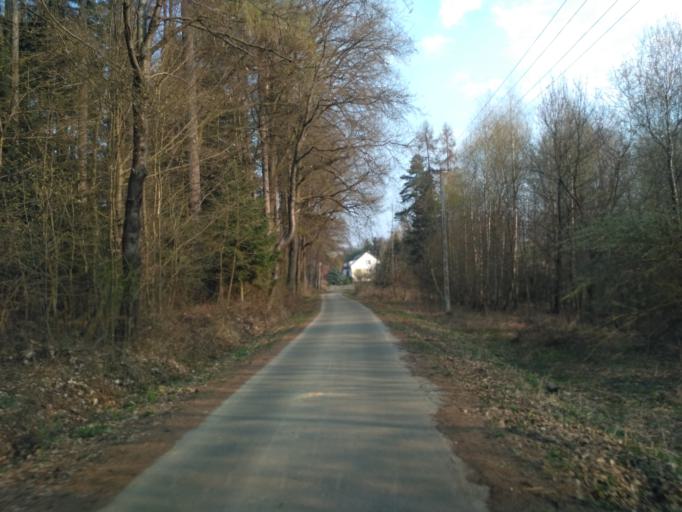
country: PL
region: Subcarpathian Voivodeship
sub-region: Powiat strzyzowski
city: Wisniowa
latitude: 49.8824
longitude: 21.6349
